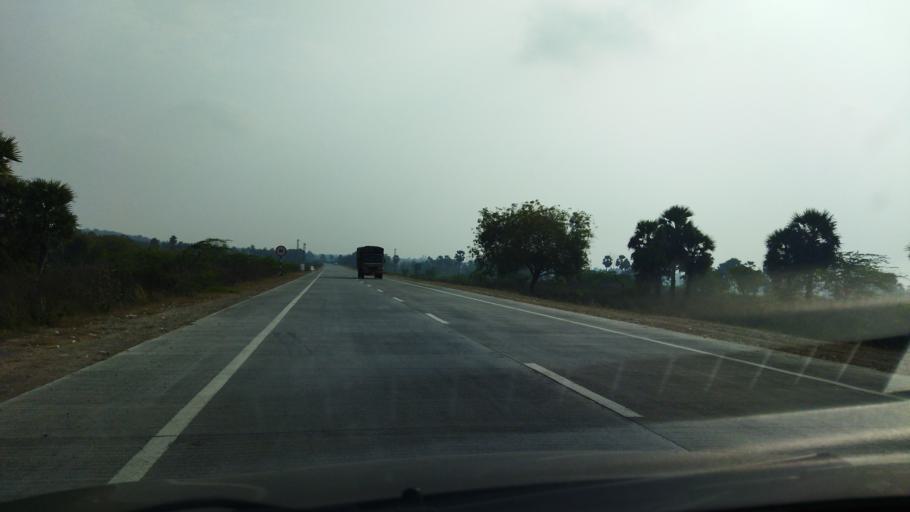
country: IN
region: Telangana
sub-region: Nalgonda
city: Nalgonda
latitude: 17.1775
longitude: 79.4022
